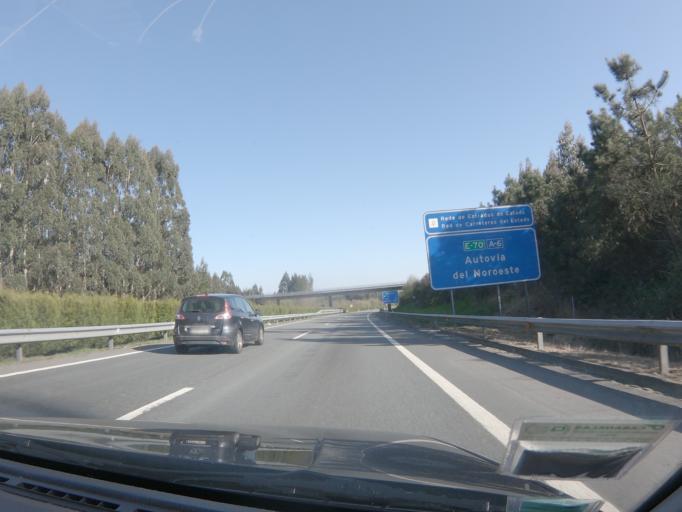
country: ES
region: Galicia
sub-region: Provincia da Coruna
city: Aranga
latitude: 43.2098
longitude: -8.0431
